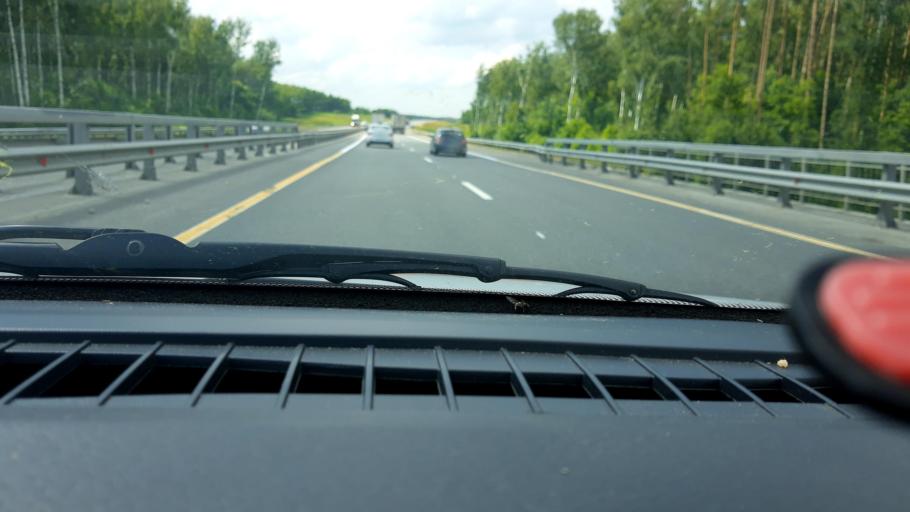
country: RU
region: Nizjnij Novgorod
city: Afonino
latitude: 56.1071
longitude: 43.9888
